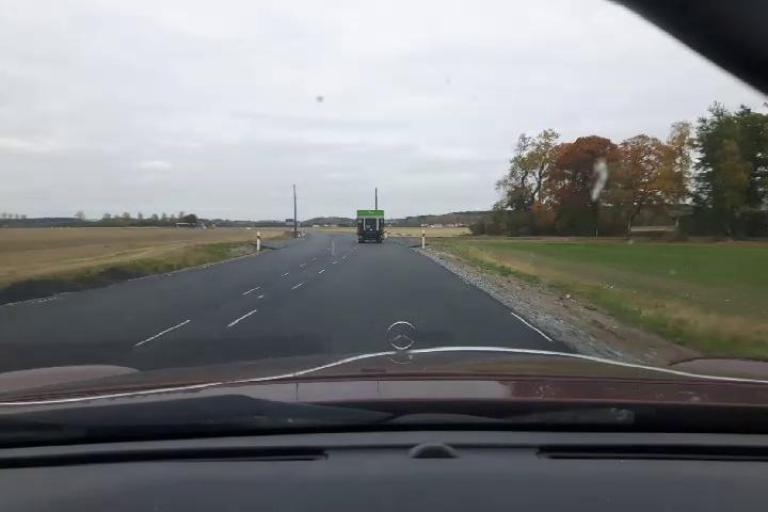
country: SE
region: Uppsala
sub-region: Enkopings Kommun
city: Enkoping
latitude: 59.6176
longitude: 17.0394
